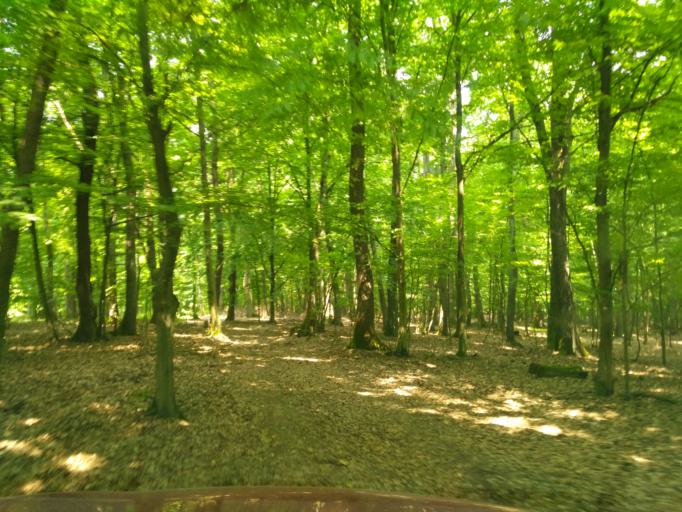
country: SK
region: Kosicky
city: Moldava nad Bodvou
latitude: 48.6542
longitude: 21.0343
